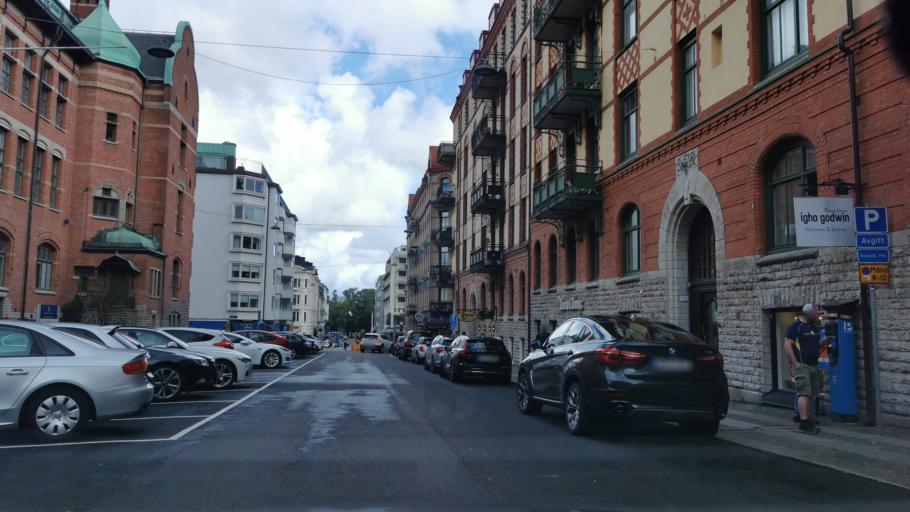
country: SE
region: Vaestra Goetaland
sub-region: Goteborg
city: Goeteborg
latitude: 57.6990
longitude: 11.9741
